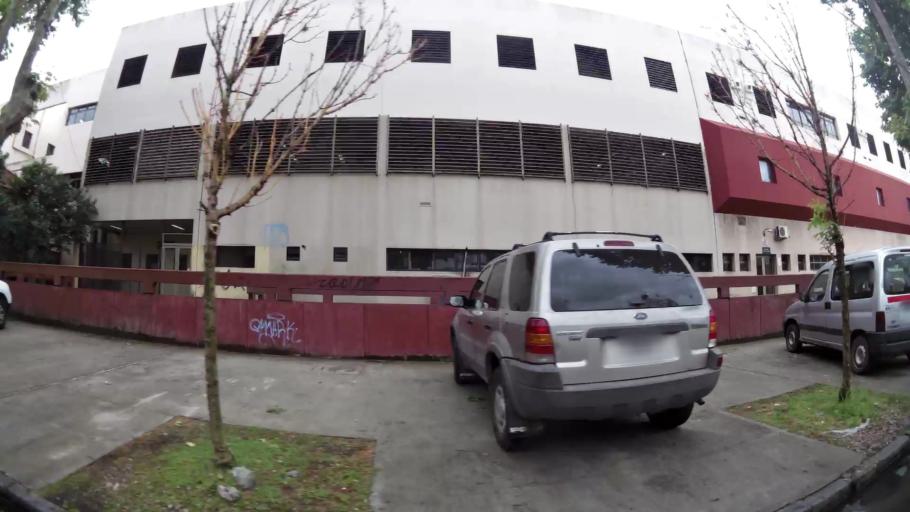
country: AR
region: Buenos Aires
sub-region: Partido de Lomas de Zamora
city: Lomas de Zamora
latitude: -34.7629
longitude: -58.3934
